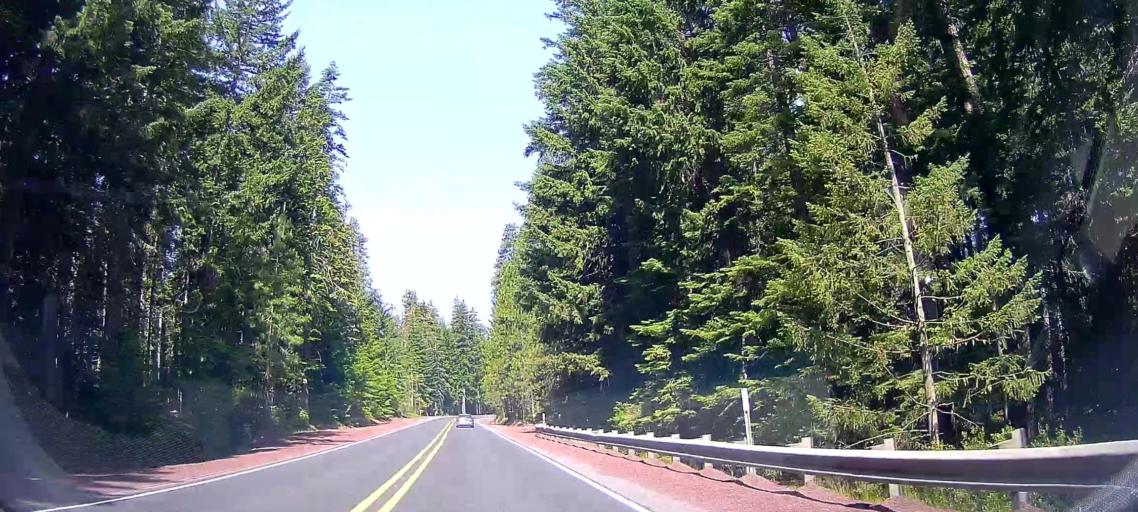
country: US
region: Oregon
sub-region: Clackamas County
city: Mount Hood Village
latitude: 45.1262
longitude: -121.5909
